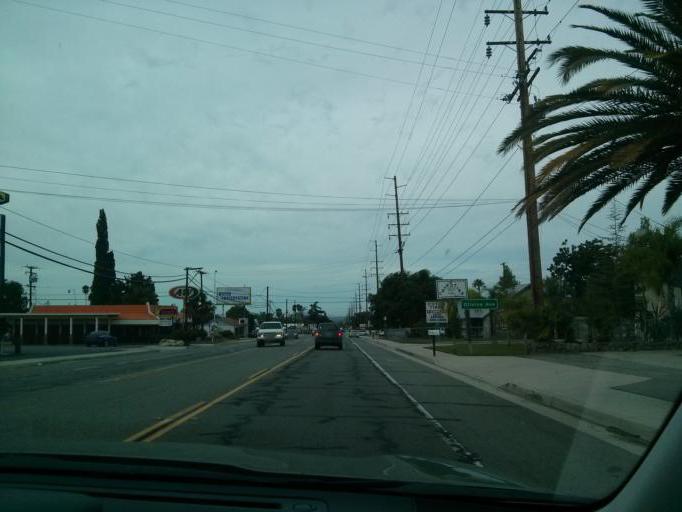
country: US
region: California
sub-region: San Bernardino County
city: Mentone
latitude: 34.0700
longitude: -117.1272
